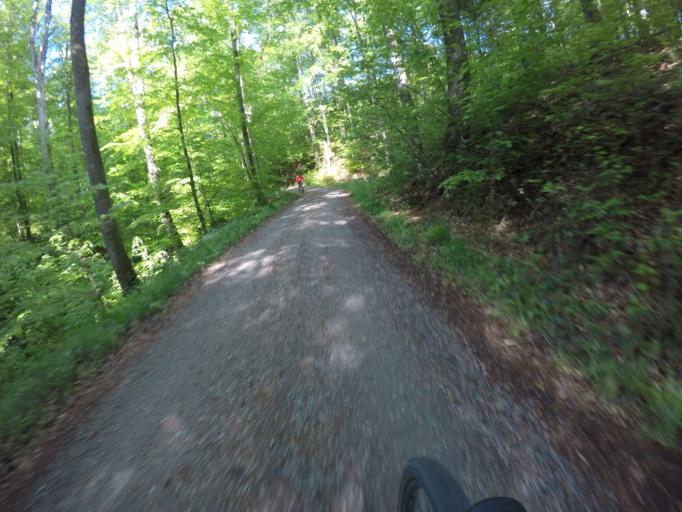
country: DE
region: Baden-Wuerttemberg
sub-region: Tuebingen Region
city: Dettenhausen
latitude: 48.5892
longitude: 9.1047
